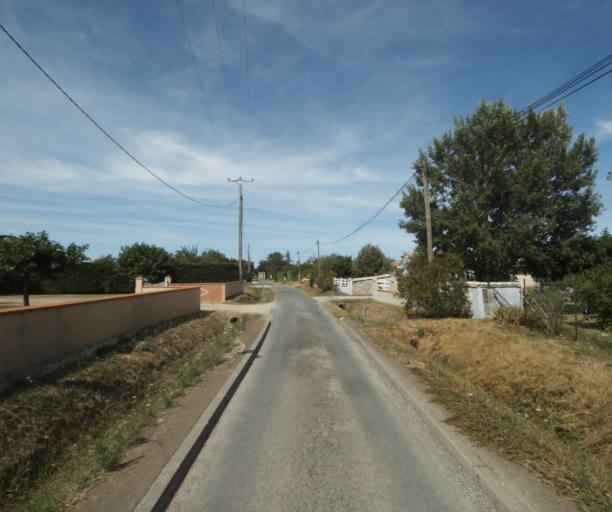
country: FR
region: Midi-Pyrenees
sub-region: Departement de la Haute-Garonne
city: Revel
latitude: 43.5082
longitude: 2.0325
